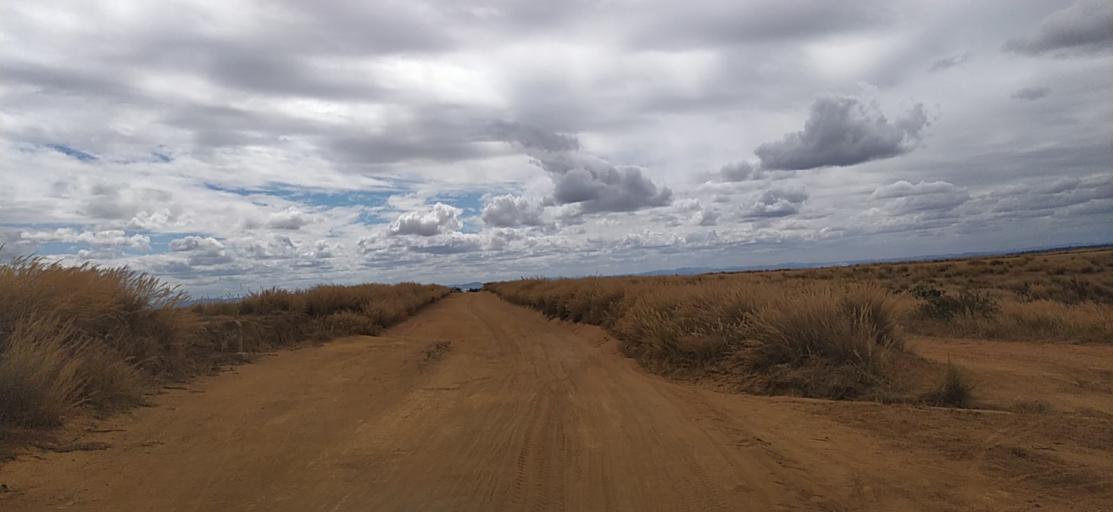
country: MG
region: Alaotra Mangoro
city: Ambatondrazaka
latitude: -17.9091
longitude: 48.2632
